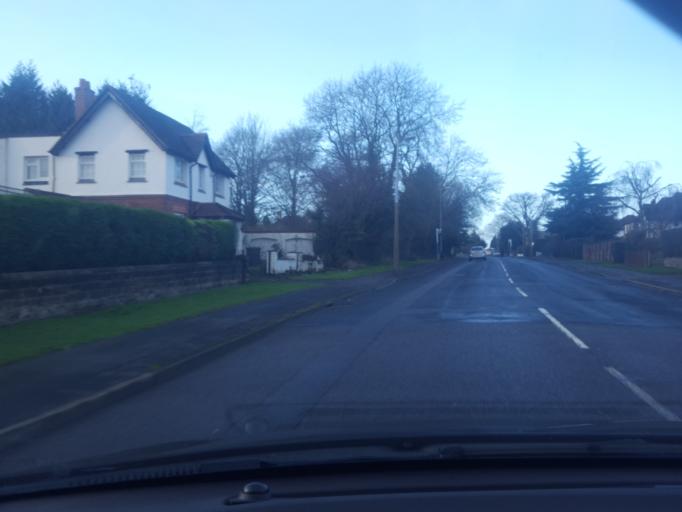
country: GB
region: England
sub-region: Staffordshire
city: Codsall
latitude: 52.6081
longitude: -2.1621
